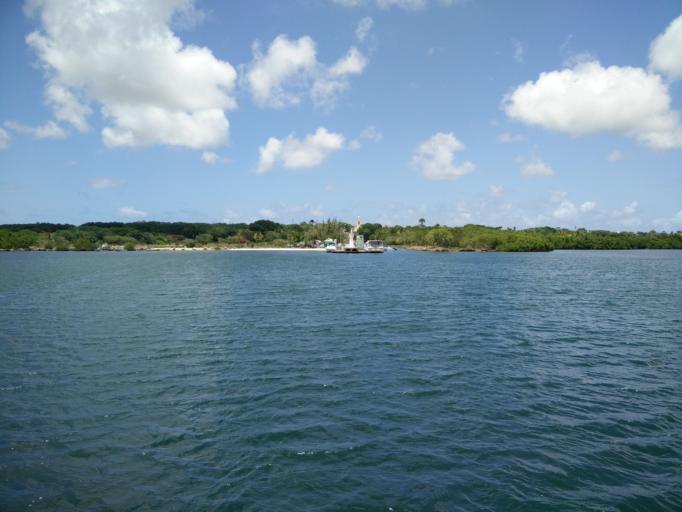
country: GP
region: Guadeloupe
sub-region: Guadeloupe
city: Petit-Canal
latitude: 16.3777
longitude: -61.4984
